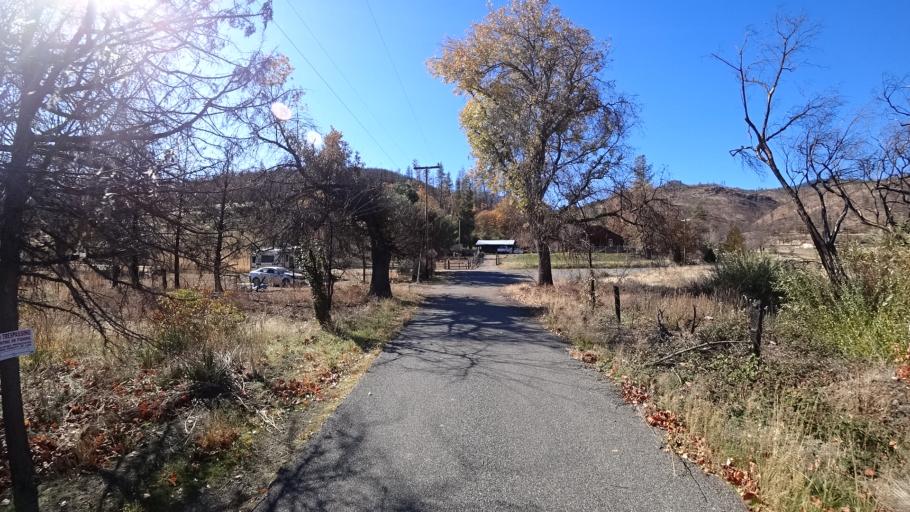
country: US
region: California
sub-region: Siskiyou County
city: Yreka
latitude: 41.9322
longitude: -122.5882
